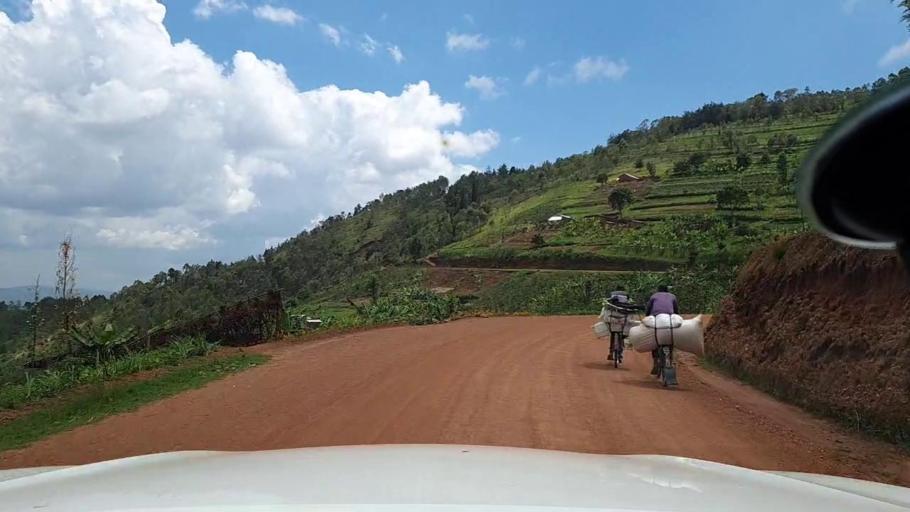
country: RW
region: Kigali
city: Kigali
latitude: -1.7814
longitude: 29.8410
